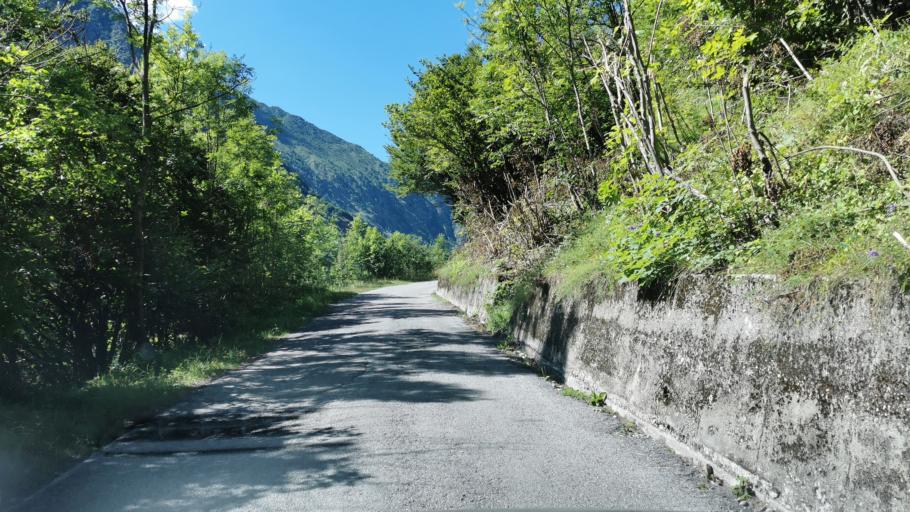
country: IT
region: Piedmont
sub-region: Provincia di Cuneo
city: Entracque
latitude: 44.2040
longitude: 7.3694
